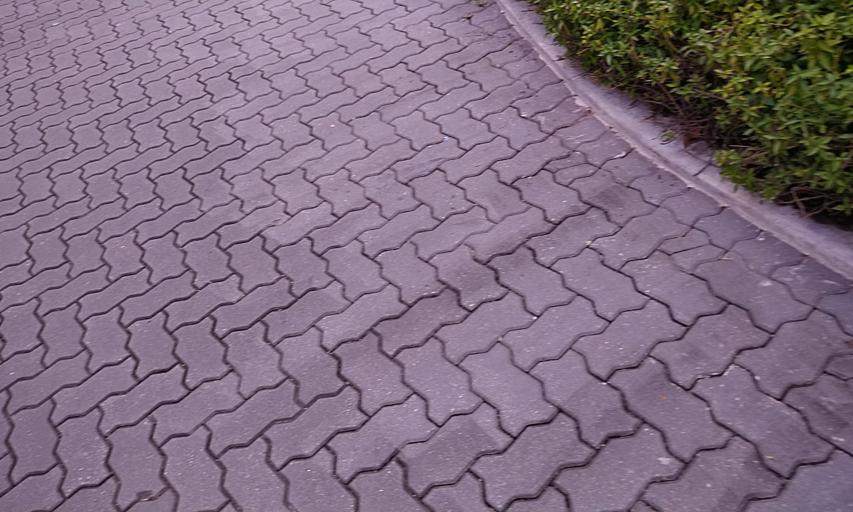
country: SG
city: Singapore
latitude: 1.2871
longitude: 103.8140
